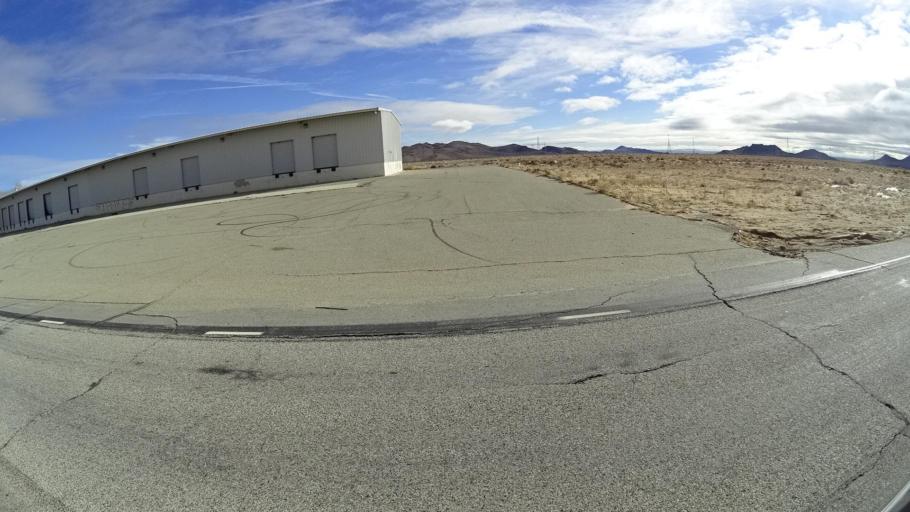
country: US
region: California
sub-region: Kern County
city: Rosamond
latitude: 34.9204
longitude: -118.2915
